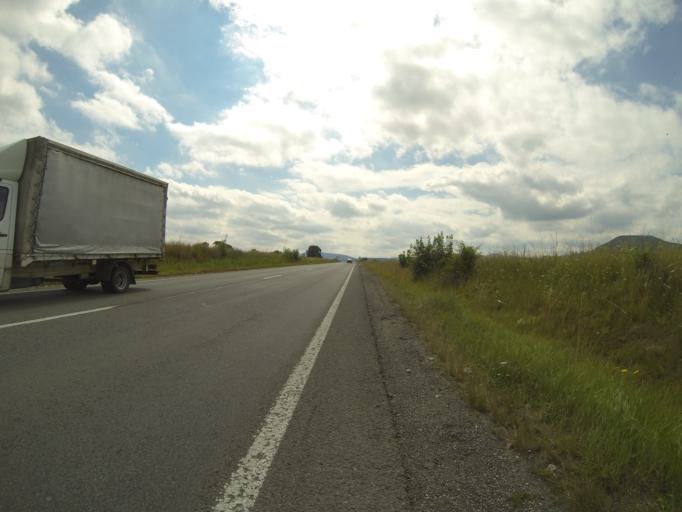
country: RO
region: Brasov
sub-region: Comuna Hoghiz
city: Hoghiz
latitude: 45.9779
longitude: 25.3296
